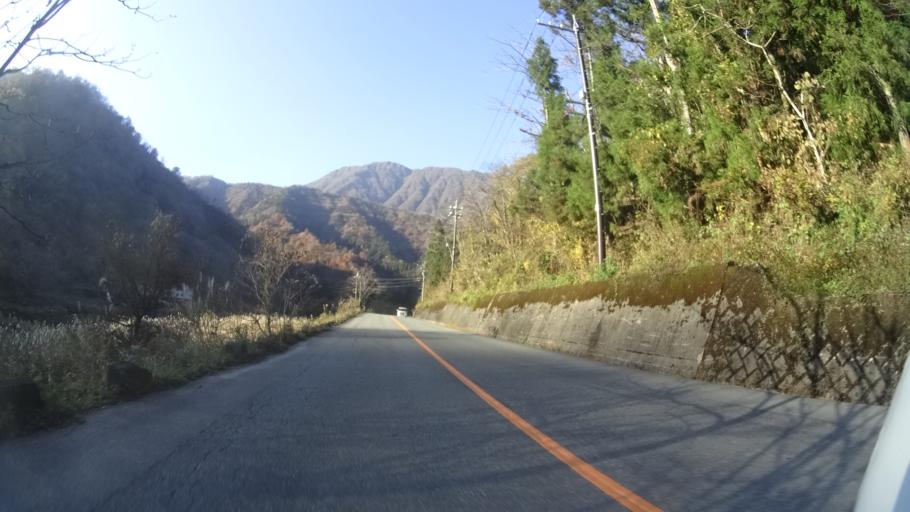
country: JP
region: Fukui
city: Ono
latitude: 35.9125
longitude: 136.6281
